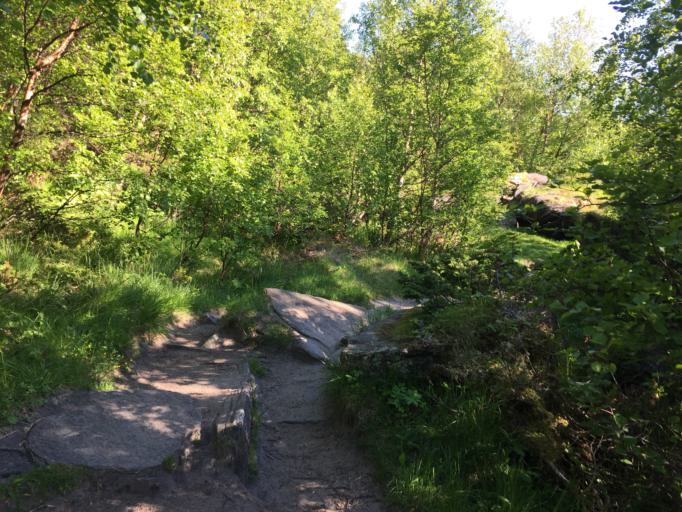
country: NO
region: Nordland
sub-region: Bodo
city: Loding
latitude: 67.4174
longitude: 14.6324
